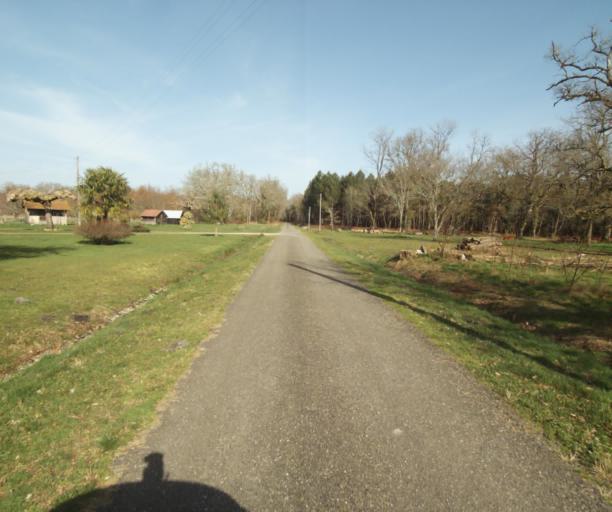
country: FR
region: Aquitaine
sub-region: Departement des Landes
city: Roquefort
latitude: 44.1529
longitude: -0.1982
